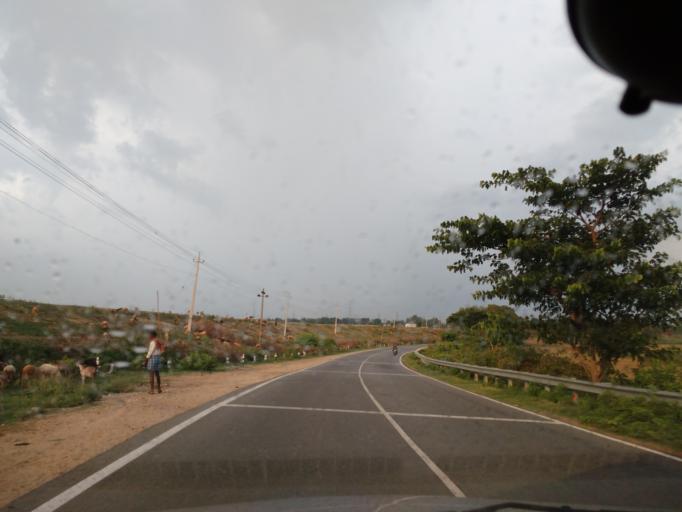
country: IN
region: Karnataka
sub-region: Tumkur
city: Tiptur
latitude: 13.2838
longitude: 76.5552
